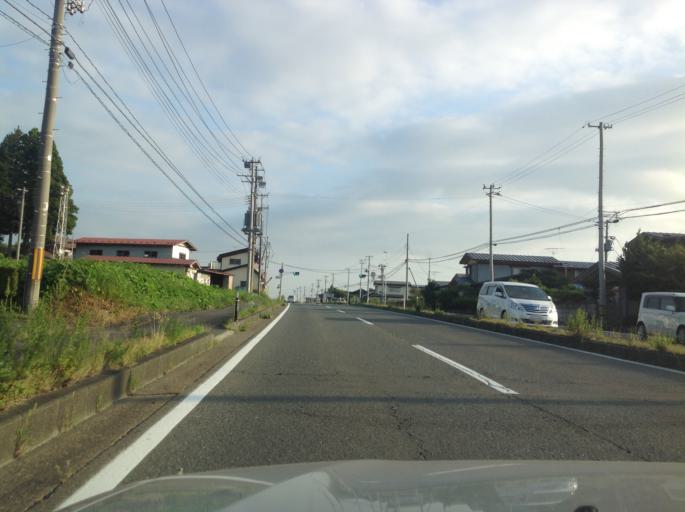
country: JP
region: Iwate
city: Hanamaki
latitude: 39.5281
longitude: 141.1633
